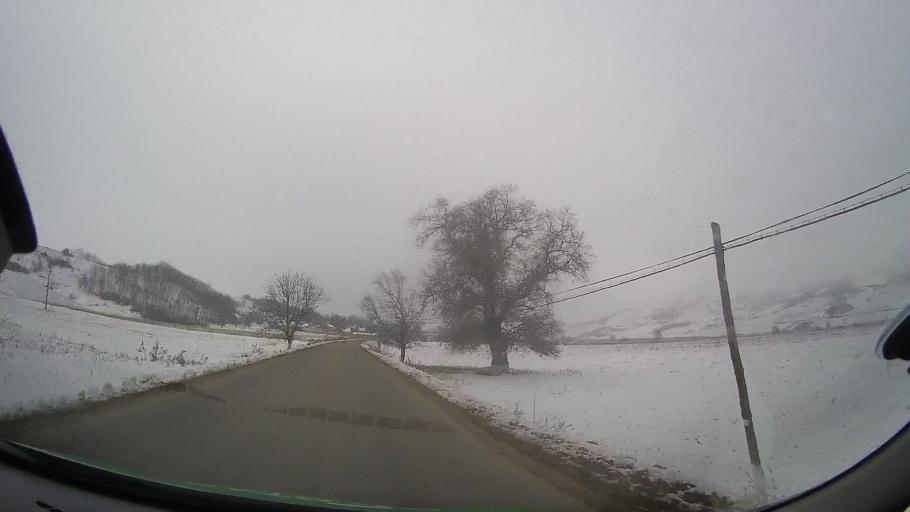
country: RO
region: Bacau
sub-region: Comuna Glavanesti
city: Frumuselu
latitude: 46.2929
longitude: 27.3008
